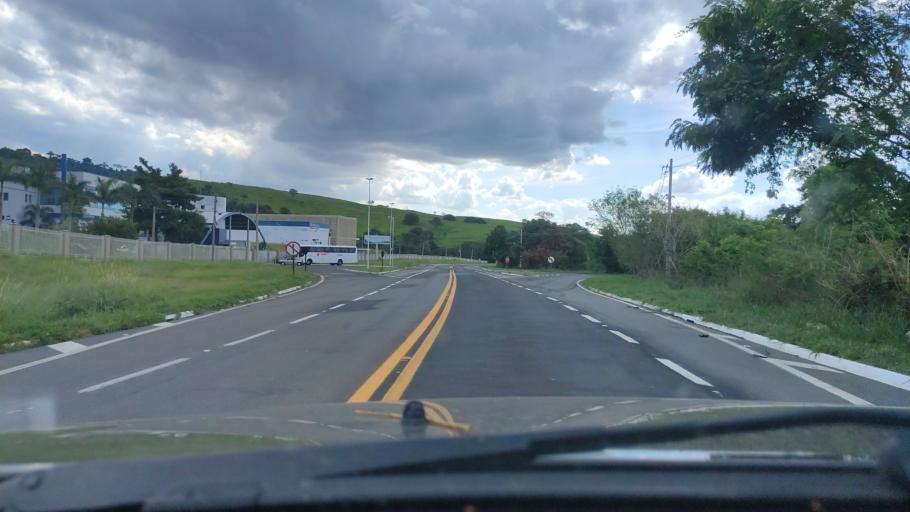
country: BR
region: Sao Paulo
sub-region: Aguas De Lindoia
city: Aguas de Lindoia
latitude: -22.4671
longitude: -46.7175
